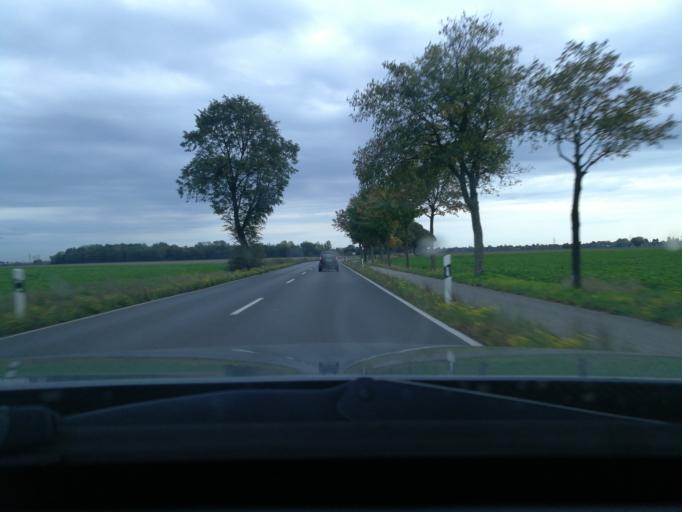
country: DE
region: North Rhine-Westphalia
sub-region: Regierungsbezirk Dusseldorf
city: Dormagen
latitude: 51.1301
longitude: 6.7572
